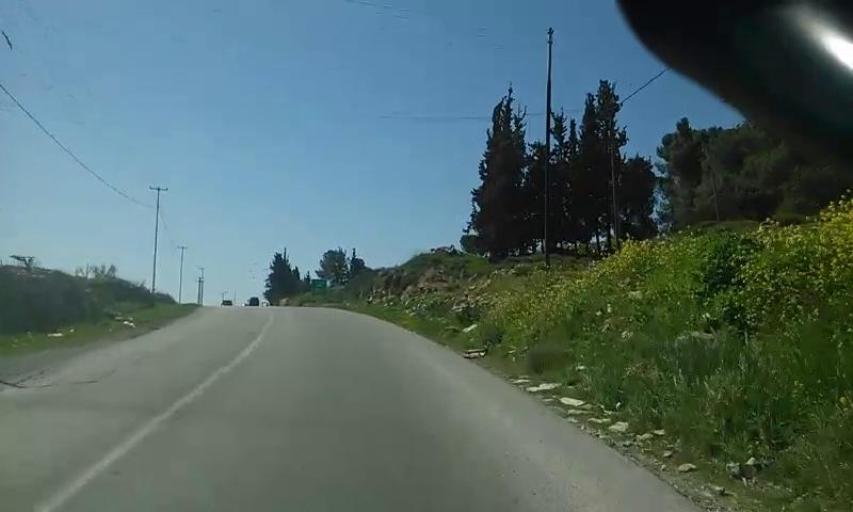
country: PS
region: West Bank
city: Bayt Ummar
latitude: 31.6034
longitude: 35.1112
